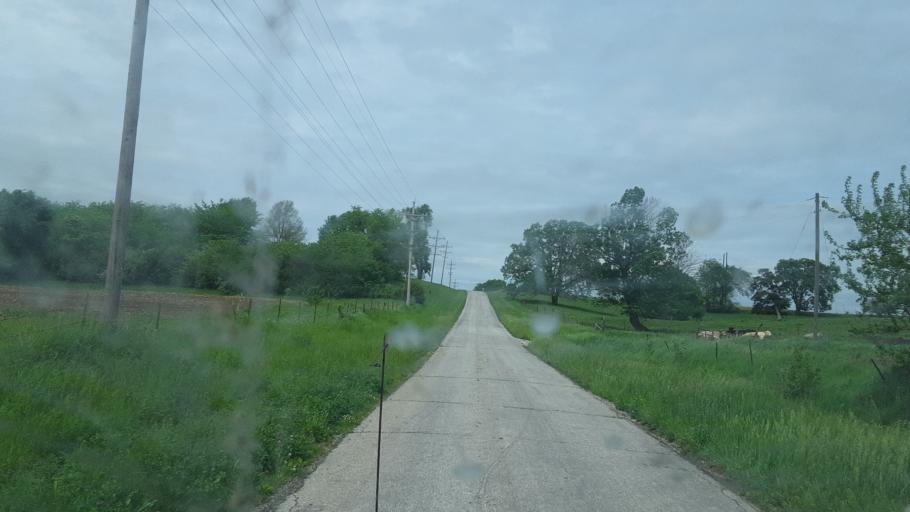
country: US
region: Missouri
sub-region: Clark County
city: Kahoka
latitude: 40.4239
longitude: -91.5846
